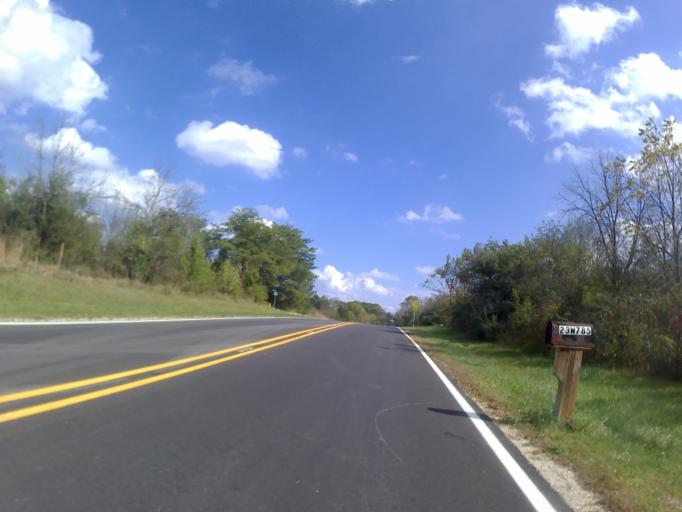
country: US
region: Illinois
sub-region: DuPage County
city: Woodridge
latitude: 41.7422
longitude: -88.0825
